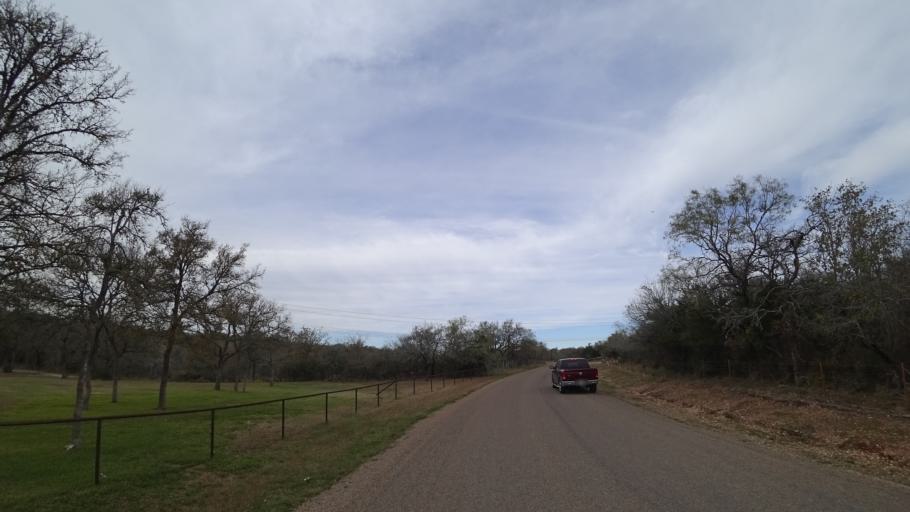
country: US
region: Texas
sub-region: Travis County
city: Garfield
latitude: 30.1095
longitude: -97.5626
